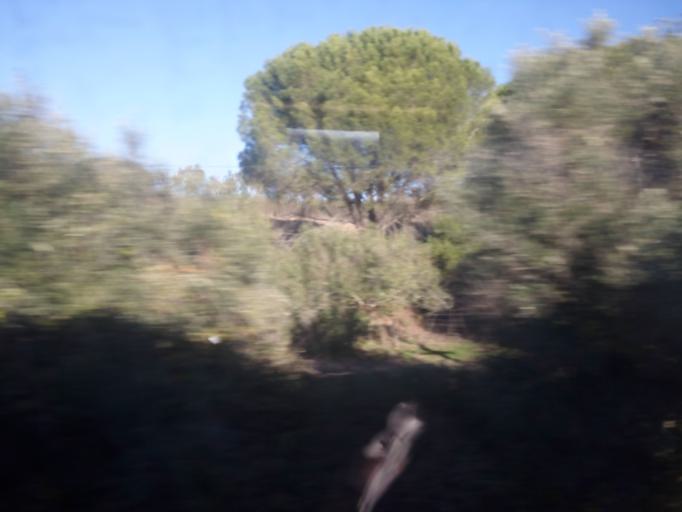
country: PT
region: Faro
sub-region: Silves
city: Sao Bartolomeu de Messines
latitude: 37.3096
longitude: -8.3174
